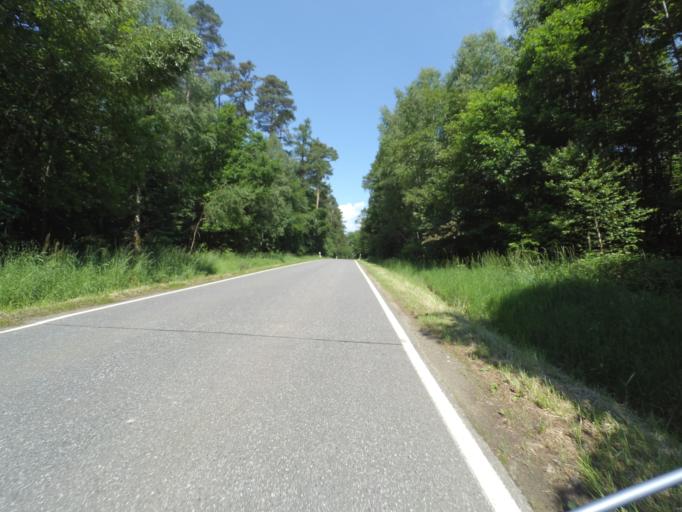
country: DE
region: Rheinland-Pfalz
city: Spesenroth
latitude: 50.0577
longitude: 7.4534
